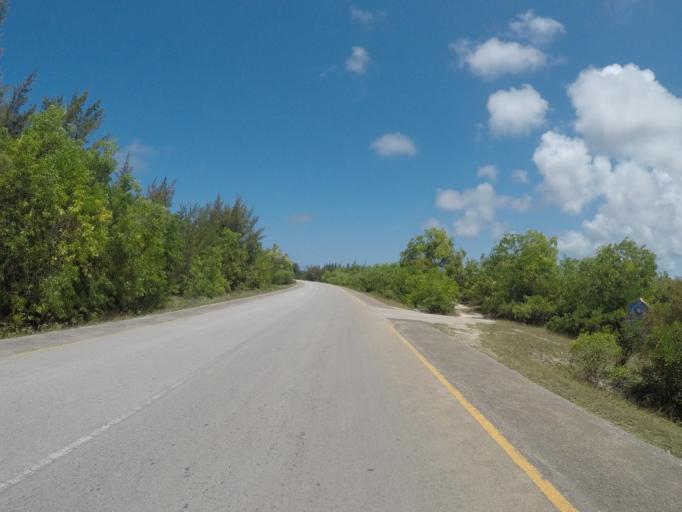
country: TZ
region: Zanzibar Central/South
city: Nganane
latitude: -6.3906
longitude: 39.5586
